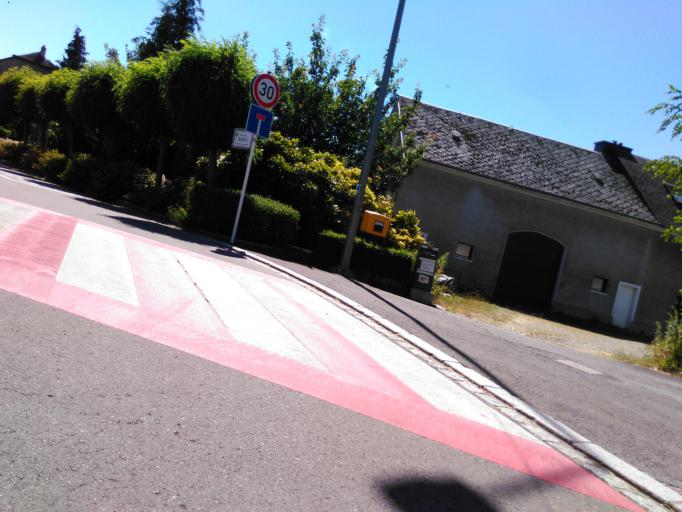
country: LU
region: Luxembourg
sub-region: Canton d'Esch-sur-Alzette
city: Leudelange
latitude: 49.5645
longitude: 6.0651
